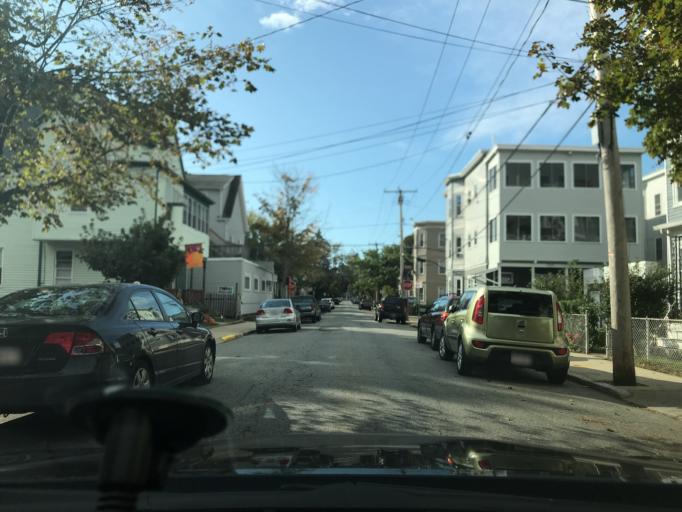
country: US
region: Massachusetts
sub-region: Middlesex County
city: Arlington
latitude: 42.3963
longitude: -71.1342
